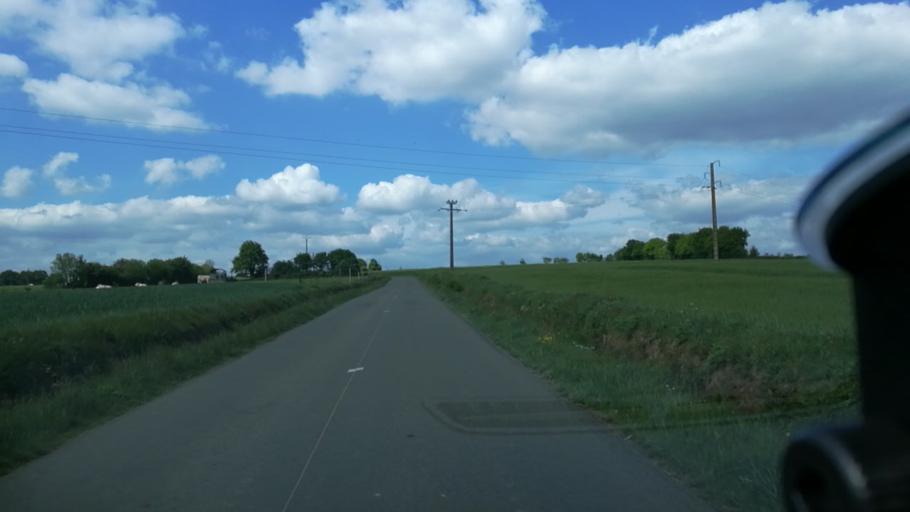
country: FR
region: Brittany
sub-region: Departement d'Ille-et-Vilaine
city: Martigne-Ferchaud
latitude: 47.8433
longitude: -1.3241
